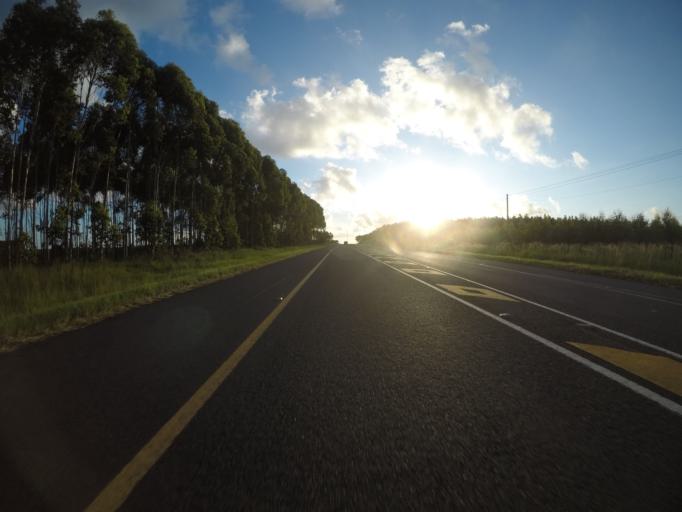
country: ZA
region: KwaZulu-Natal
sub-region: uThungulu District Municipality
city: Empangeni
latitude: -28.6987
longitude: 31.9756
